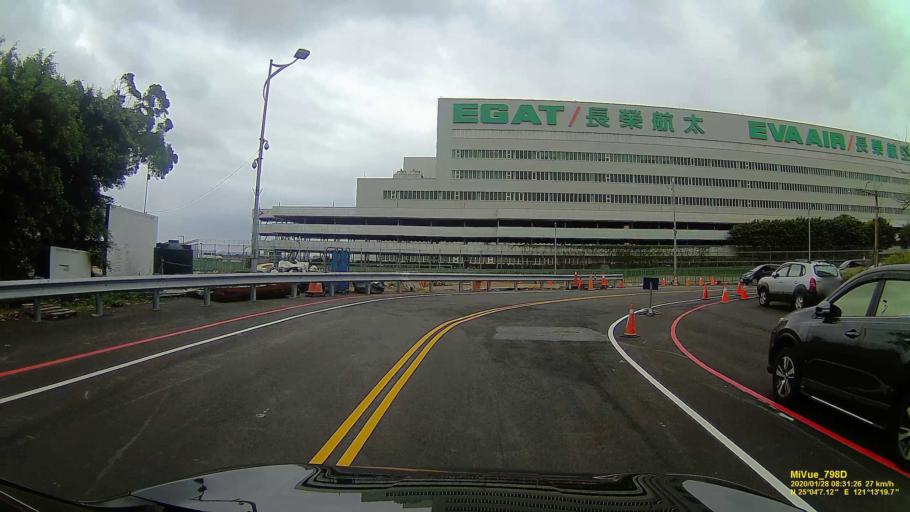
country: TW
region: Taiwan
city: Taoyuan City
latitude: 25.0685
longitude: 121.2220
